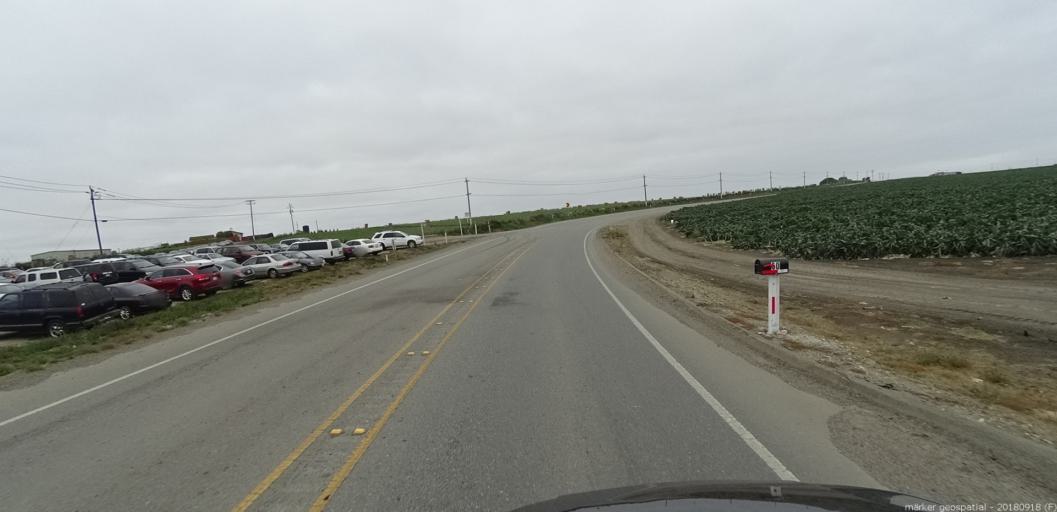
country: US
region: California
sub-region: Monterey County
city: Castroville
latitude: 36.7426
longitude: -121.7322
